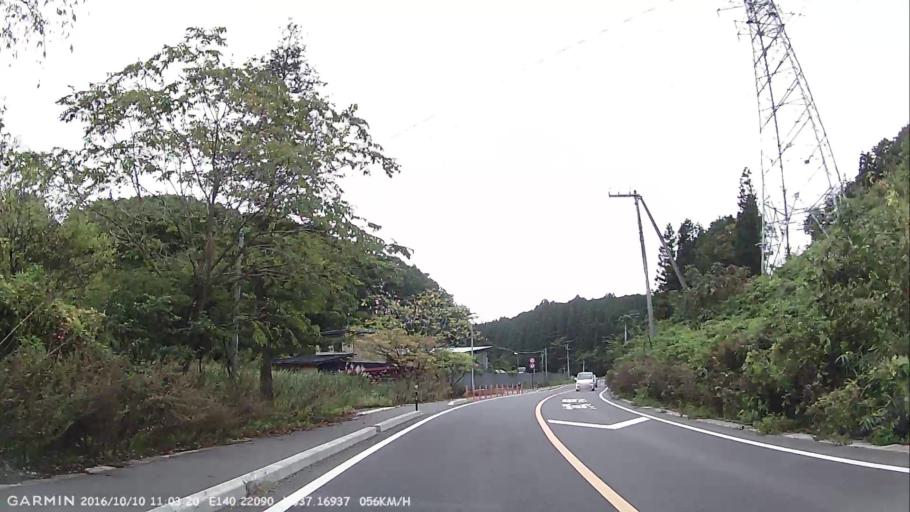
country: JP
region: Fukushima
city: Sukagawa
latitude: 37.1694
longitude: 140.2209
